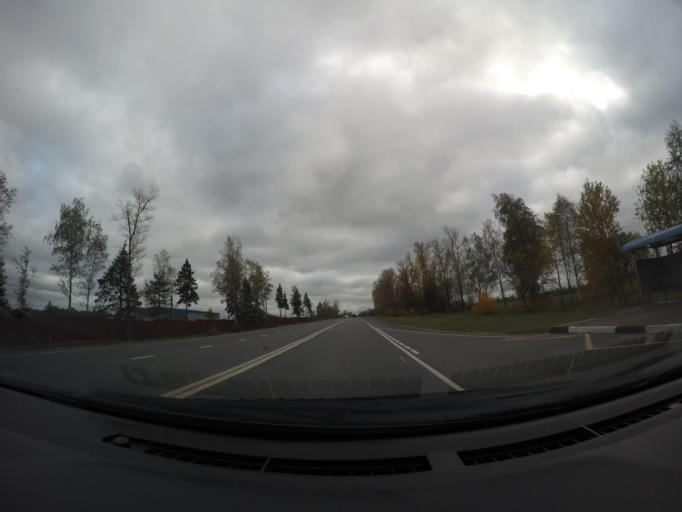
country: RU
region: Moskovskaya
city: Dorokhovo
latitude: 55.5976
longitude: 36.3609
